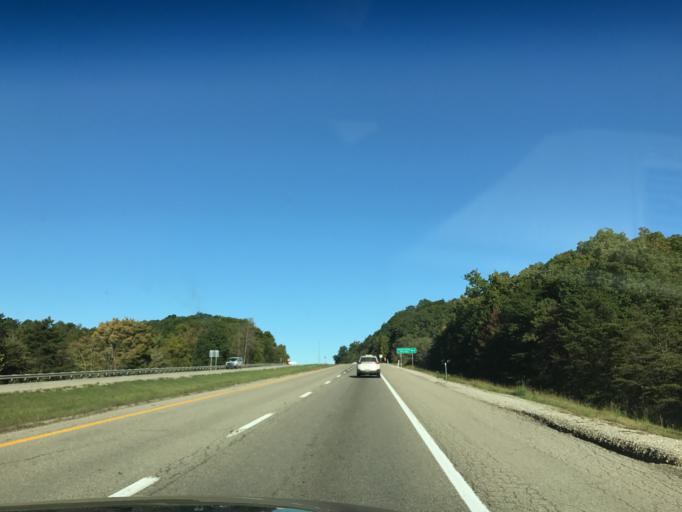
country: US
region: Ohio
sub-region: Washington County
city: Newport
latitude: 39.2521
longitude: -81.2636
